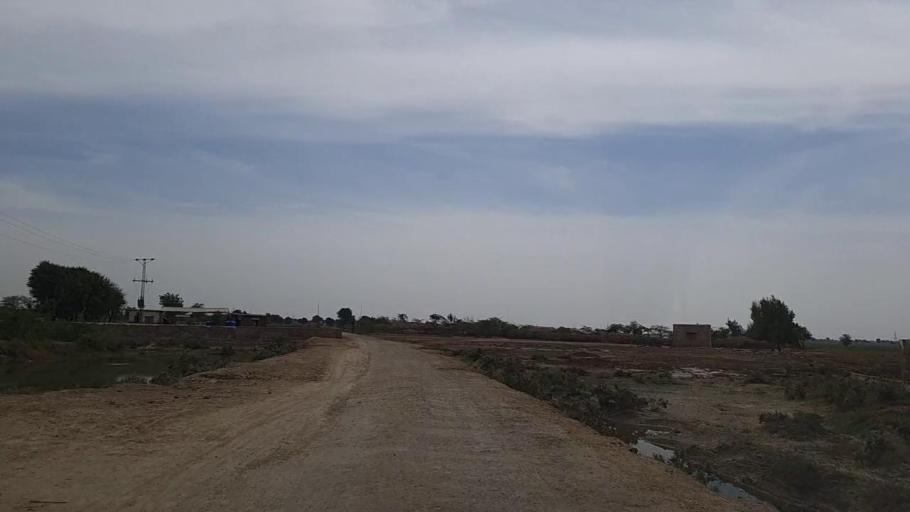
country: PK
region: Sindh
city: Samaro
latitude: 25.3059
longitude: 69.4509
